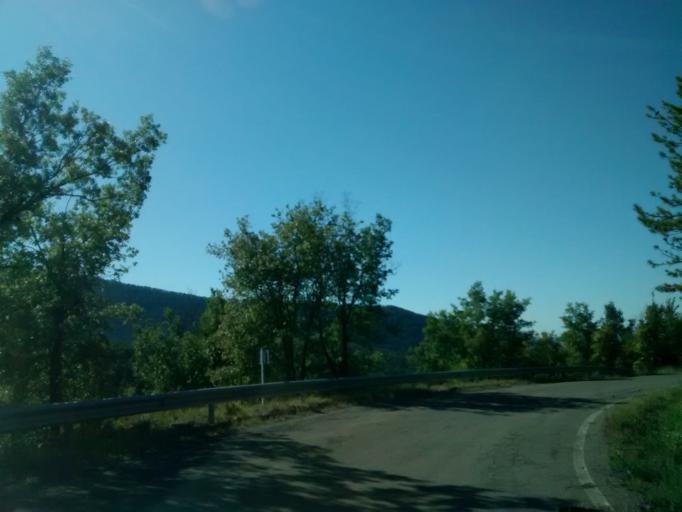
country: ES
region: Aragon
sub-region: Provincia de Huesca
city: Jaca
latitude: 42.5003
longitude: -0.5500
